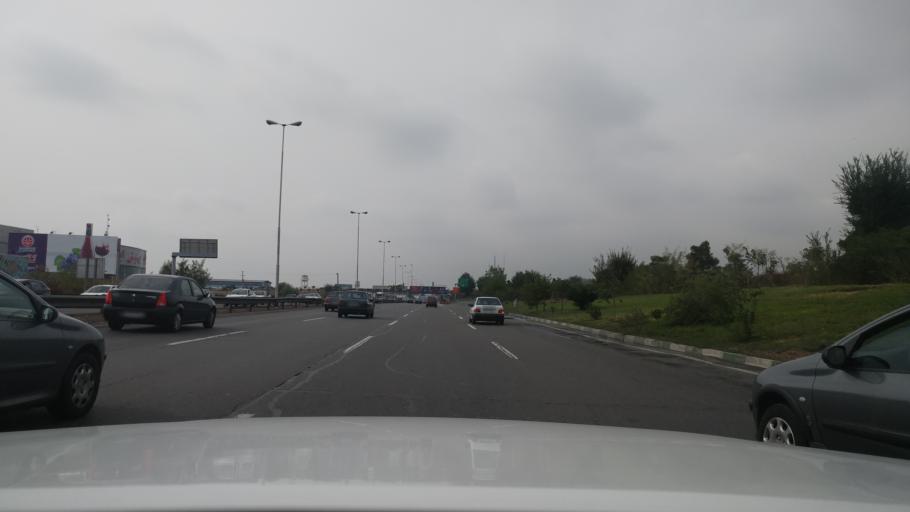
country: IR
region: Tehran
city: Shahr-e Qods
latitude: 35.7154
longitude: 51.2448
